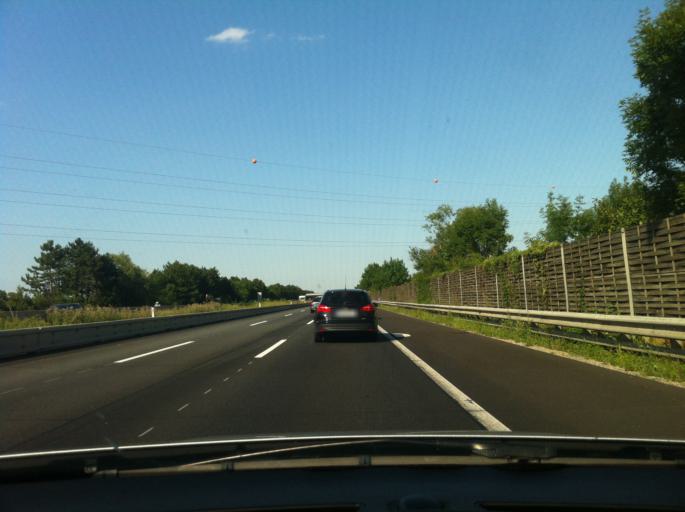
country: AT
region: Lower Austria
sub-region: Politischer Bezirk Neunkirchen
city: Breitenau
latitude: 47.7342
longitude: 16.1623
